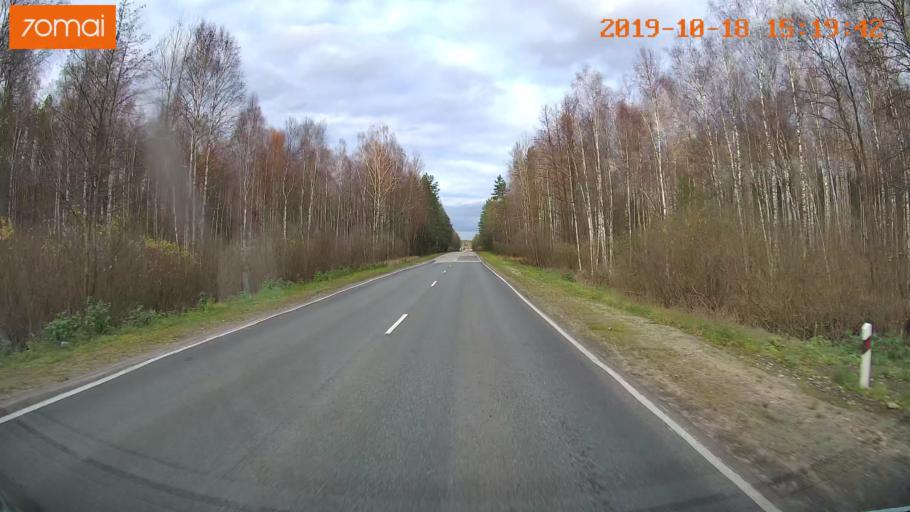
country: RU
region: Vladimir
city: Anopino
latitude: 55.6769
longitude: 40.7396
